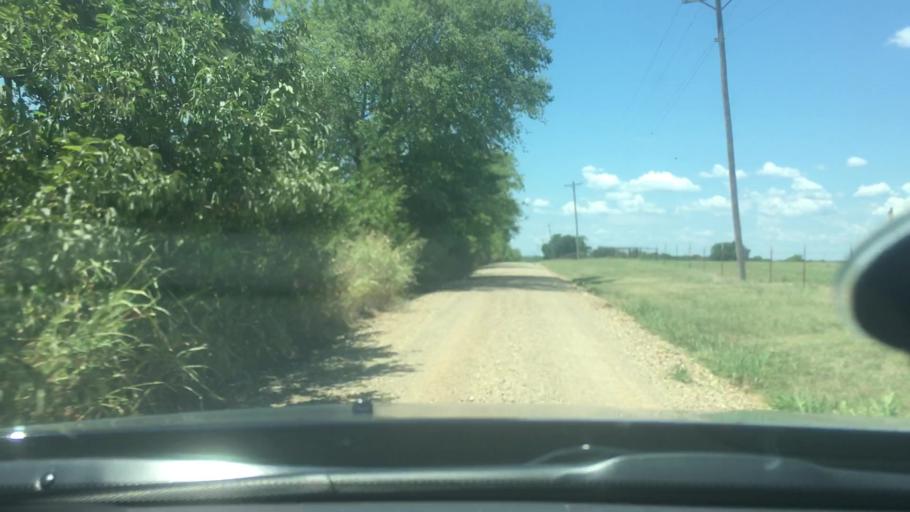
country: US
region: Oklahoma
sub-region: Bryan County
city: Durant
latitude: 33.9973
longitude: -96.1066
